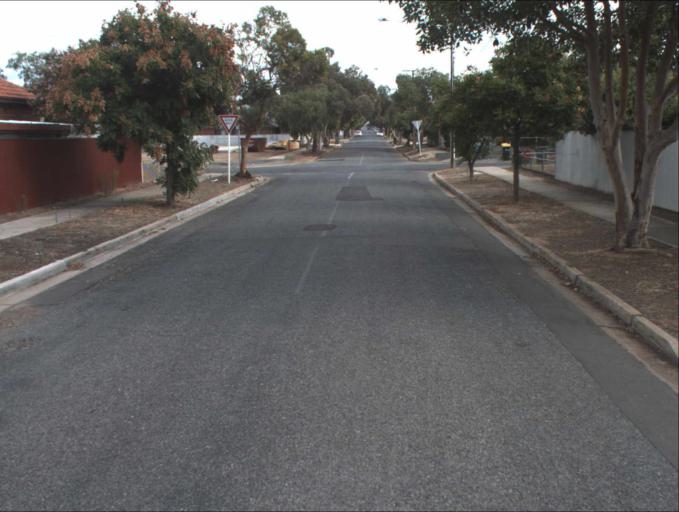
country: AU
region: South Australia
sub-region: Prospect
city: Prospect
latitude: -34.8706
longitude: 138.5877
